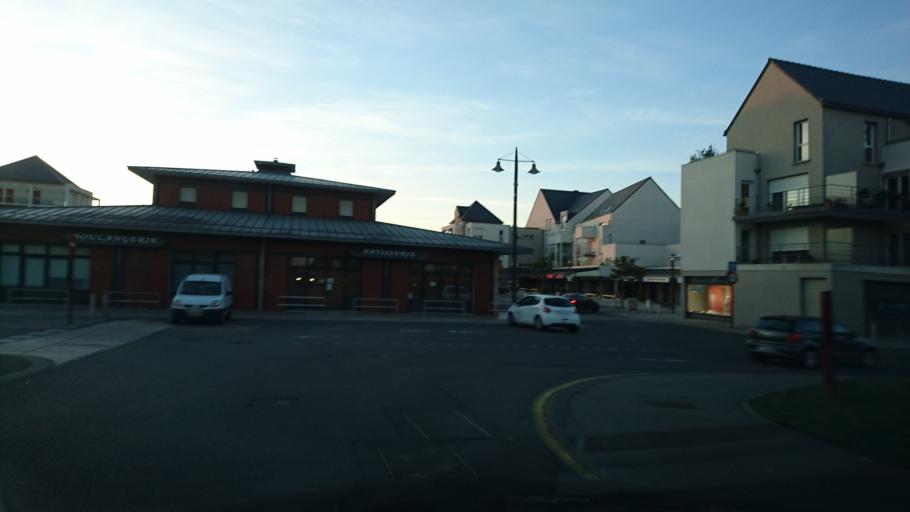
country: FR
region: Brittany
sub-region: Departement d'Ille-et-Vilaine
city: Bruz
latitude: 48.0294
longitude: -1.7583
